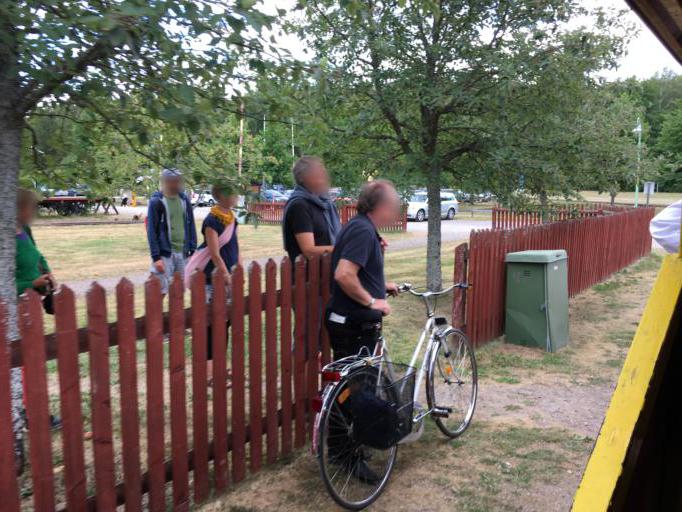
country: SE
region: OEstergoetland
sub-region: Linkopings Kommun
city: Linkoping
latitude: 58.4009
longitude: 15.5851
